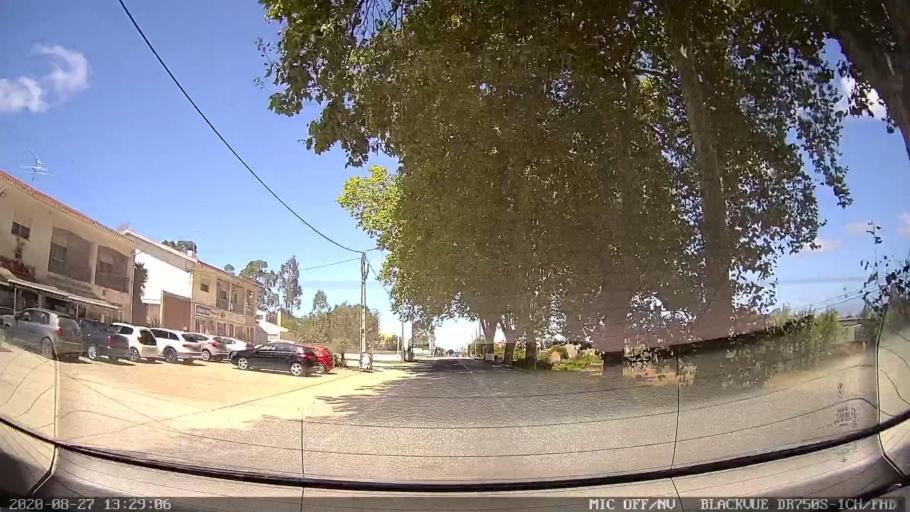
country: PT
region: Aveiro
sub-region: Vagos
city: Vagos
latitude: 40.5136
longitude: -8.6778
